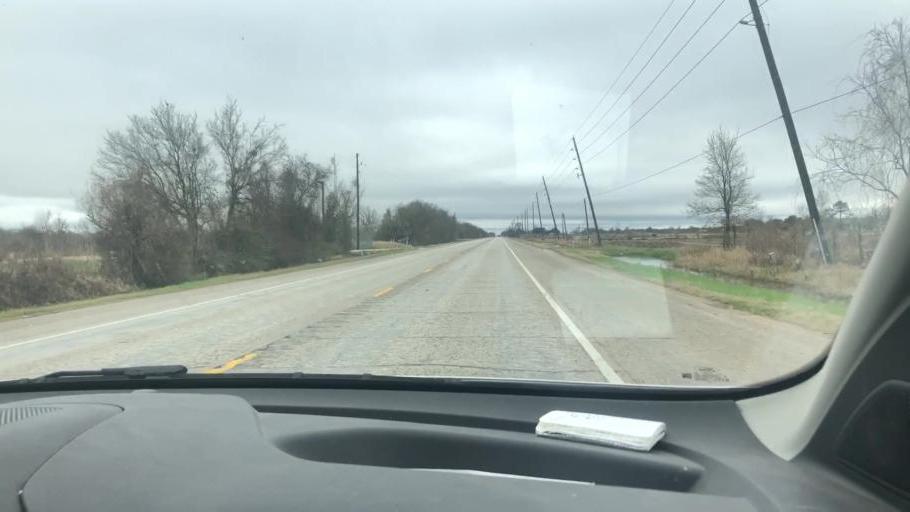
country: US
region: Texas
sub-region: Wharton County
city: Wharton
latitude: 29.2792
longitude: -96.0654
